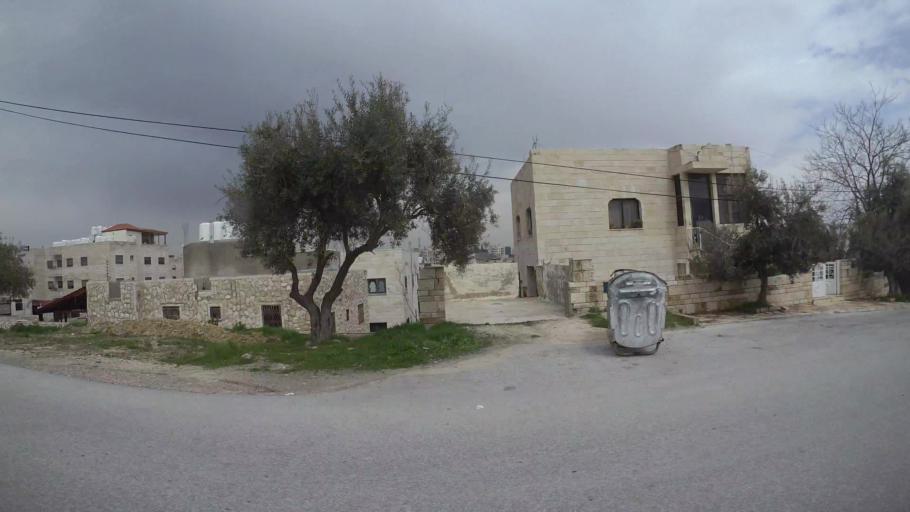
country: JO
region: Amman
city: Umm as Summaq
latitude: 31.9061
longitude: 35.8442
